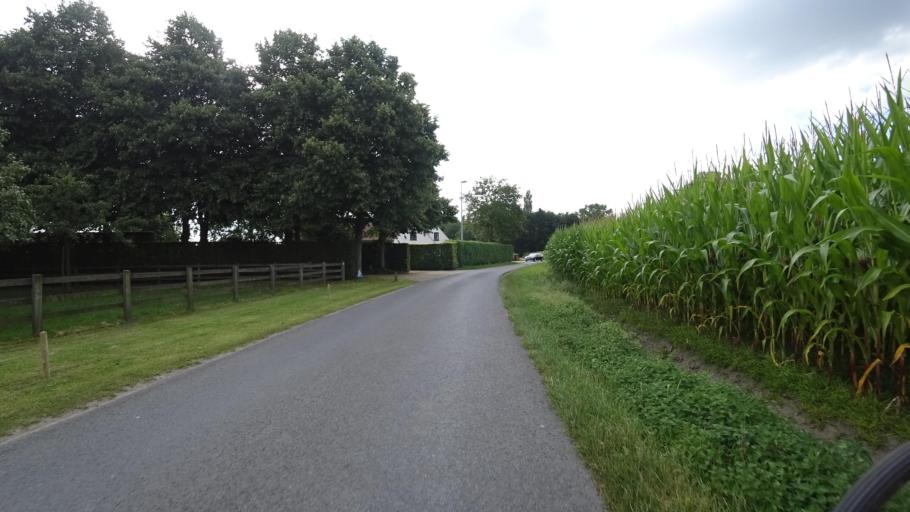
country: BE
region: Flanders
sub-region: Provincie West-Vlaanderen
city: Beernem
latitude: 51.1856
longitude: 3.3152
